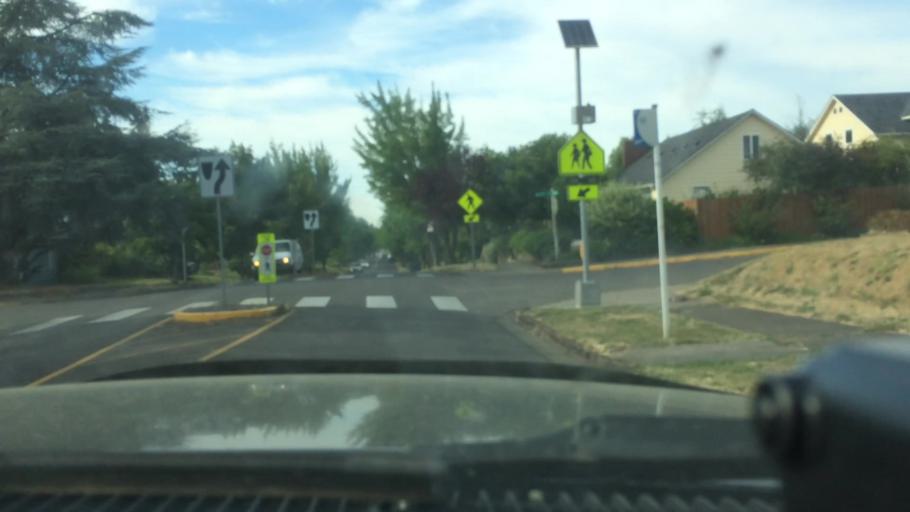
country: US
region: Oregon
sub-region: Lane County
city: Eugene
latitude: 44.0353
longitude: -123.1012
